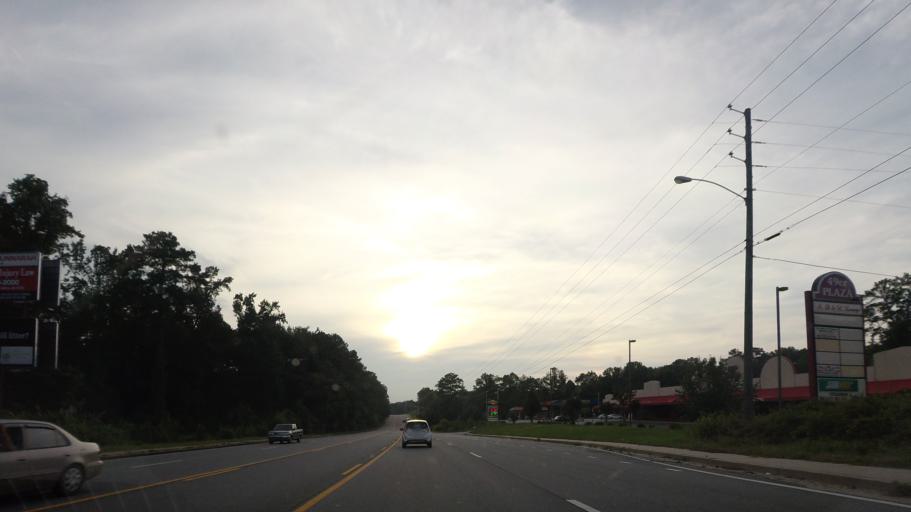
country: US
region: Georgia
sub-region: Bibb County
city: Macon
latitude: 32.8658
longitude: -83.5783
